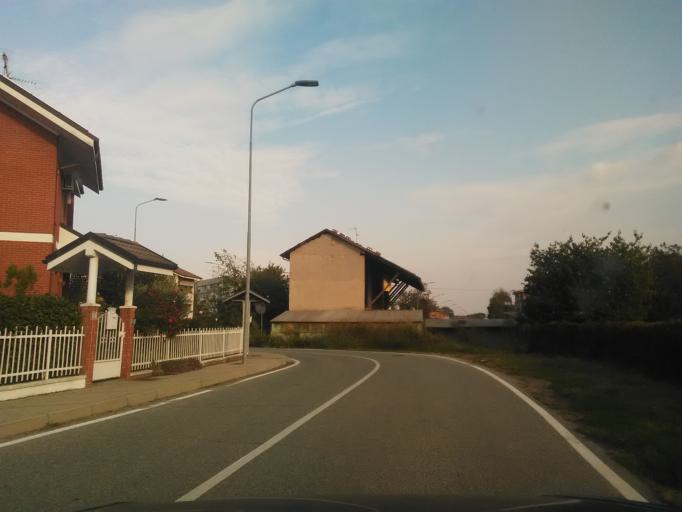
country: IT
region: Piedmont
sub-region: Provincia di Vercelli
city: Santhia
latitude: 45.3710
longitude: 8.1607
